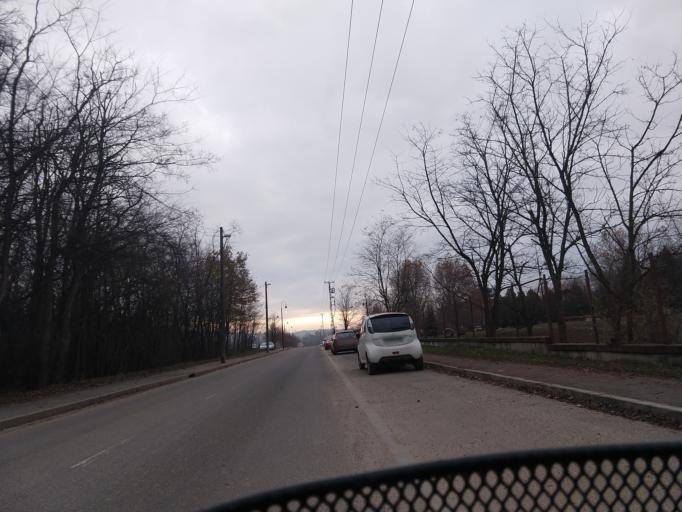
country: HU
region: Pest
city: Orbottyan
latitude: 47.6641
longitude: 19.2714
